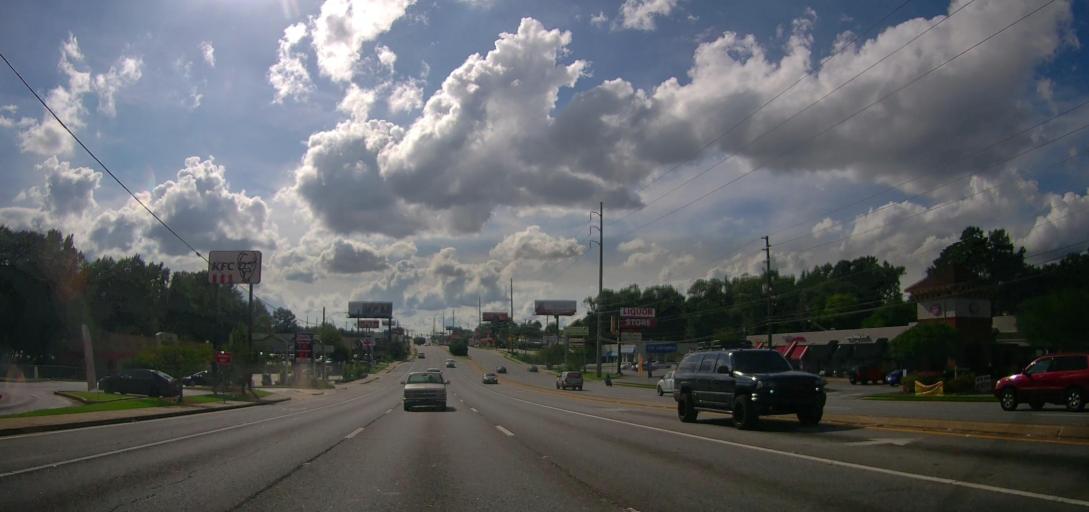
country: US
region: Georgia
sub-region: Muscogee County
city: Columbus
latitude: 32.5070
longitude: -84.9627
